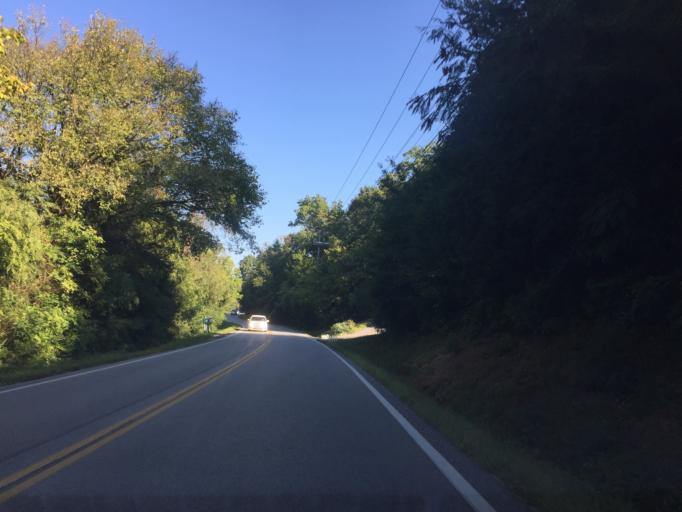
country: US
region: Tennessee
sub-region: Hamilton County
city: Harrison
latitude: 35.1155
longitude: -85.0822
